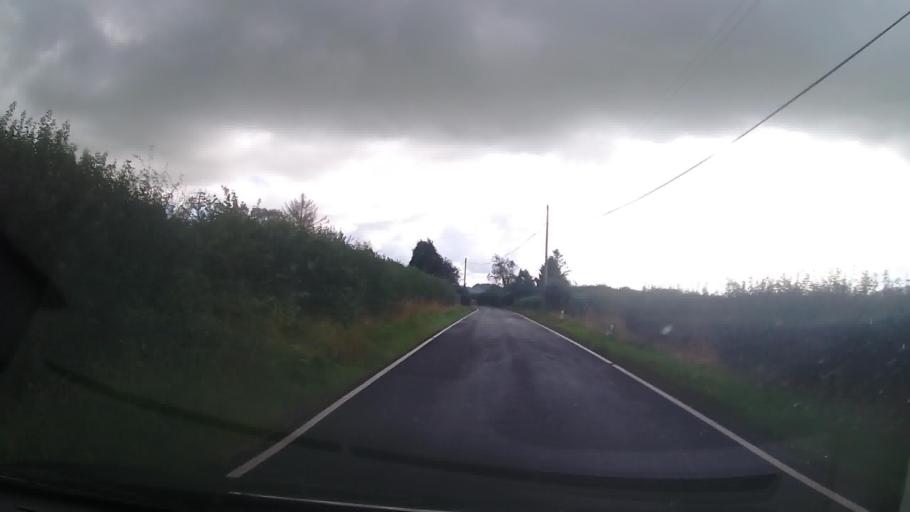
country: GB
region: England
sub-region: Shropshire
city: Norbury
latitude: 52.5854
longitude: -2.9554
